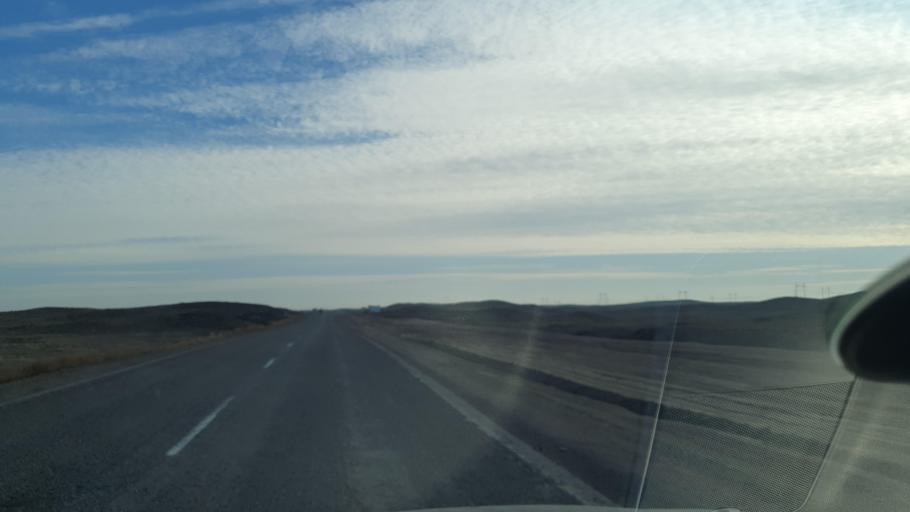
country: KZ
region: Zhambyl
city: Mynaral
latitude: 45.5300
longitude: 73.4803
